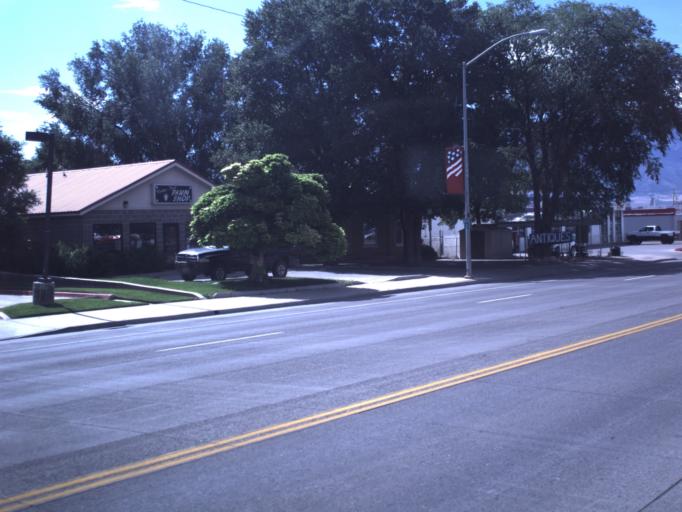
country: US
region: Utah
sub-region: Sevier County
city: Richfield
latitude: 38.7636
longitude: -112.0849
